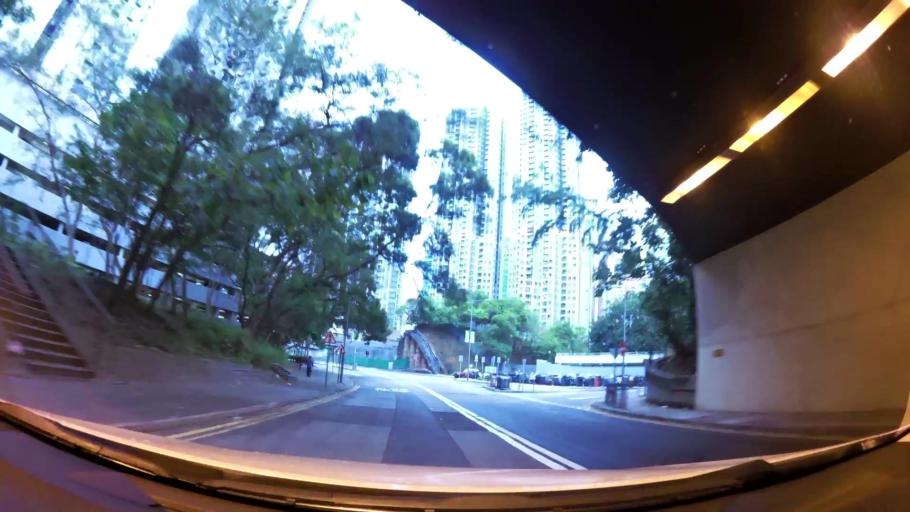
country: HK
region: Tsuen Wan
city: Tsuen Wan
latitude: 22.3622
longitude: 114.1153
